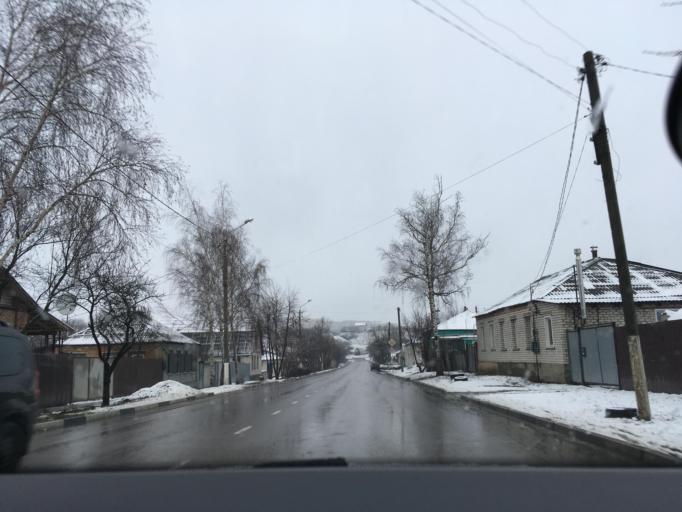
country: RU
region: Belgorod
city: Valuyki
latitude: 50.2074
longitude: 38.1079
